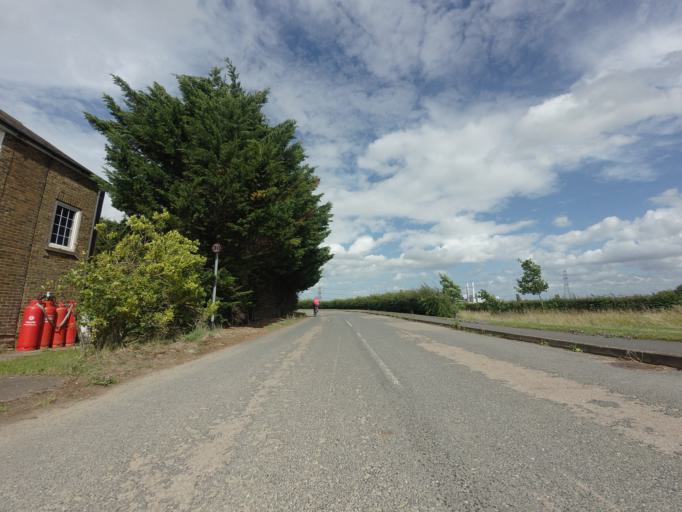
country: GB
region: England
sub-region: Kent
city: Hoo
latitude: 51.4307
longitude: 0.5896
